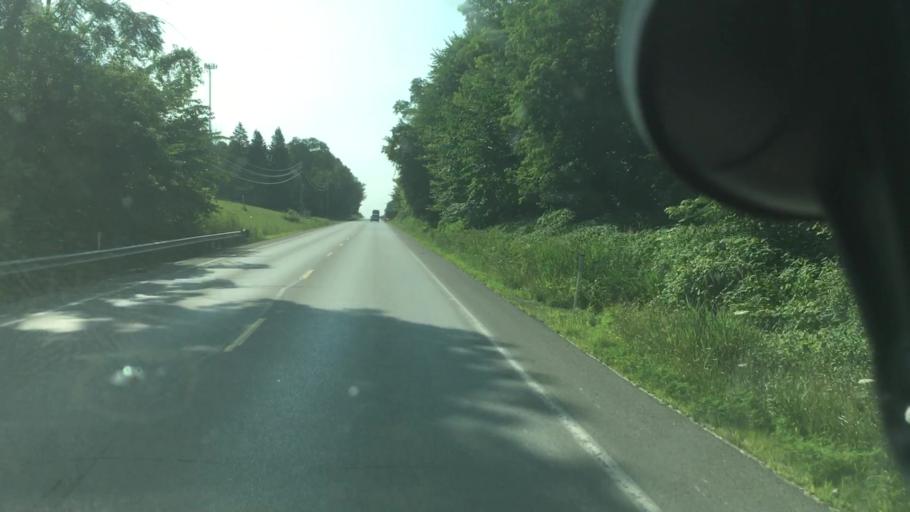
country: US
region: Pennsylvania
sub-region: Lawrence County
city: Bessemer
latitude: 41.0116
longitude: -80.4809
